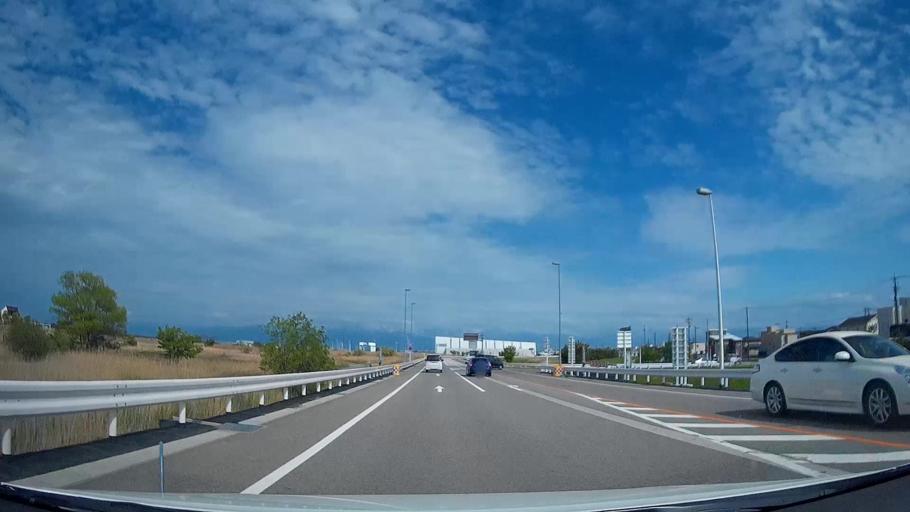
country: JP
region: Toyama
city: Kuragaki-kosugi
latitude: 36.7734
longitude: 137.1297
